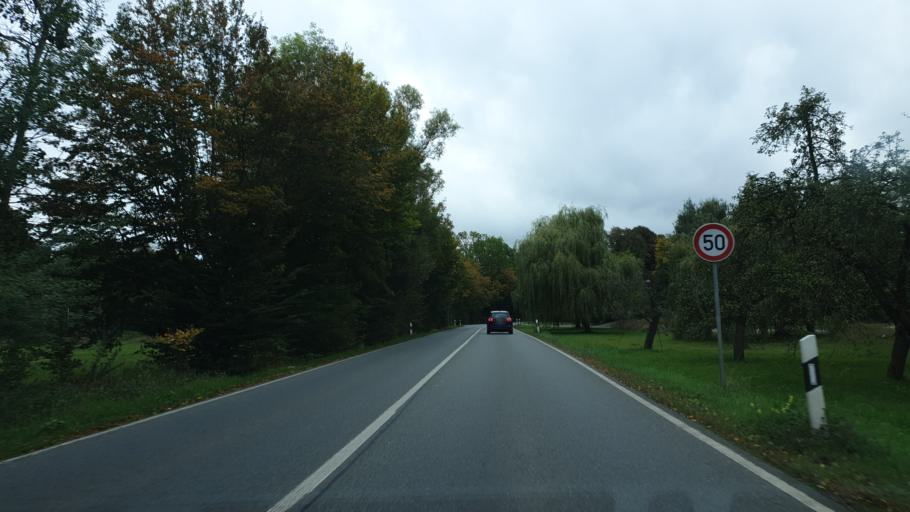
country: DE
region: Saxony
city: Glauchau
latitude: 50.8196
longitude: 12.5671
